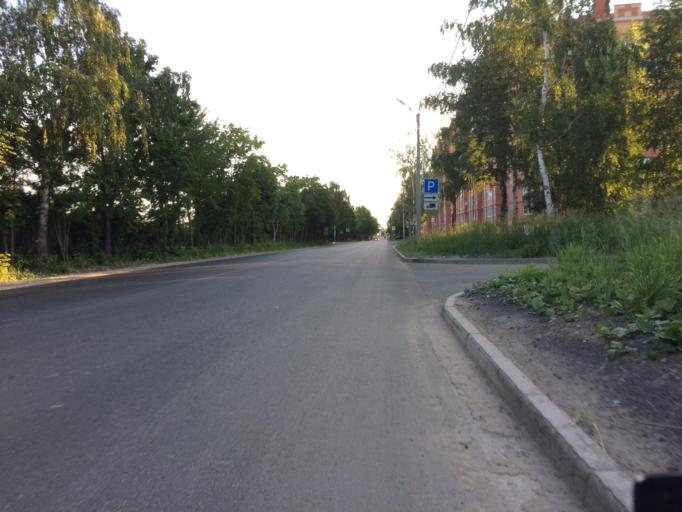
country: RU
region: Mariy-El
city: Medvedevo
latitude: 56.6437
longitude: 47.8315
